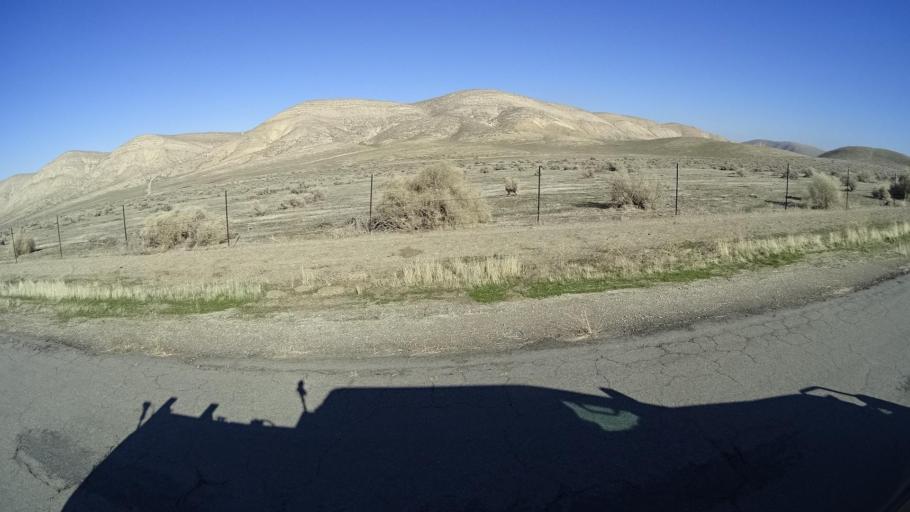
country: US
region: California
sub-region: Kern County
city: Maricopa
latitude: 34.9947
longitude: -119.3947
